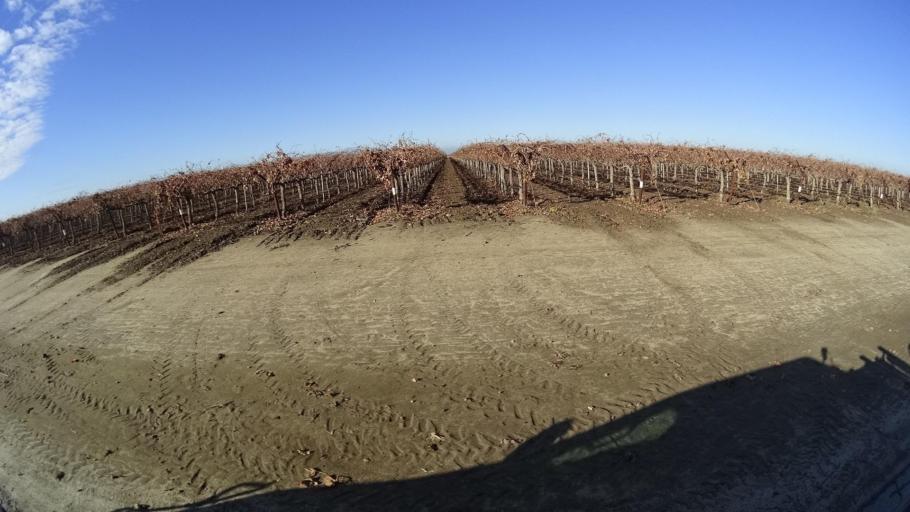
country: US
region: California
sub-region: Kern County
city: Delano
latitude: 35.7233
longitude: -119.2942
